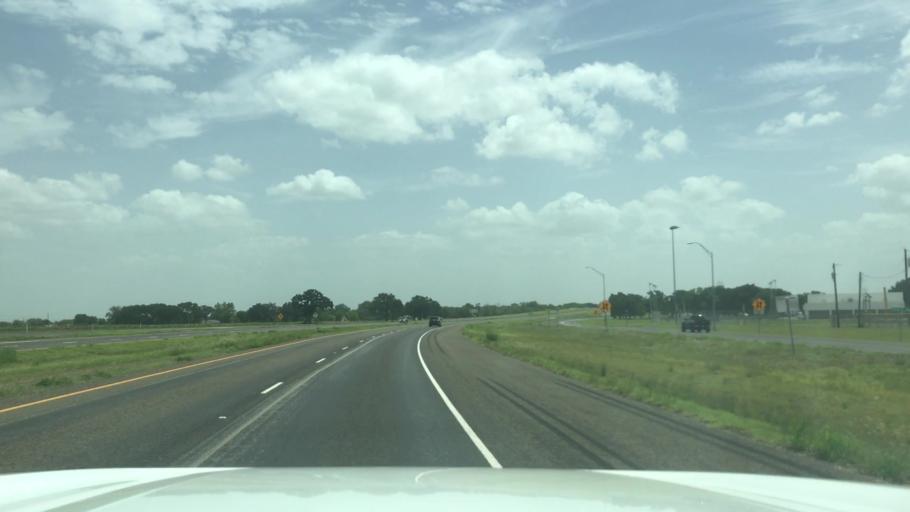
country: US
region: Texas
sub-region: Falls County
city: Marlin
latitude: 31.3131
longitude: -96.8756
